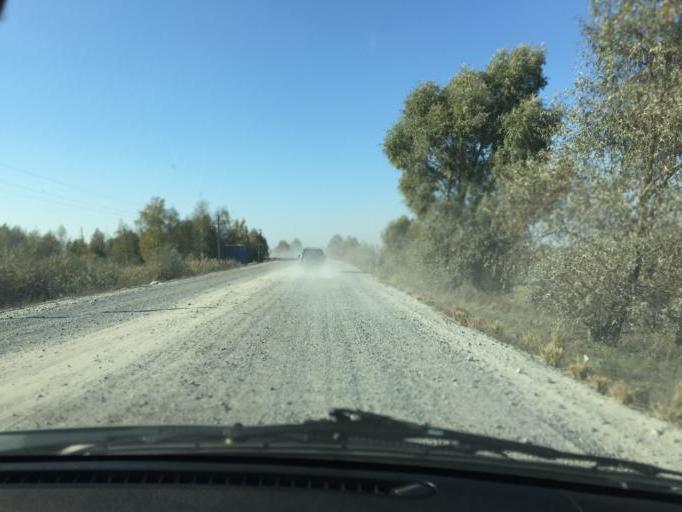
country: BY
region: Gomel
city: Turaw
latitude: 52.0705
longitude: 27.8141
